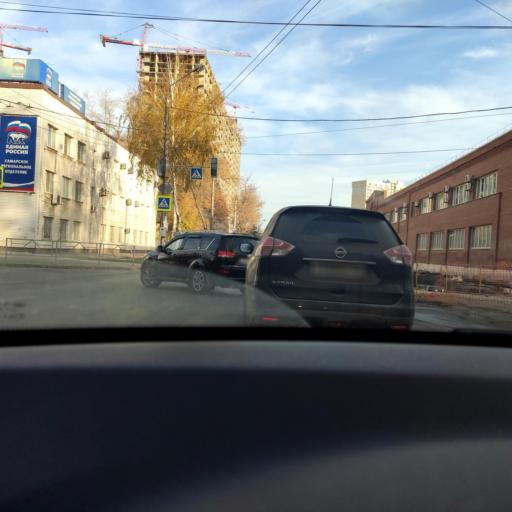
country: RU
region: Samara
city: Samara
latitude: 53.2035
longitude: 50.1783
